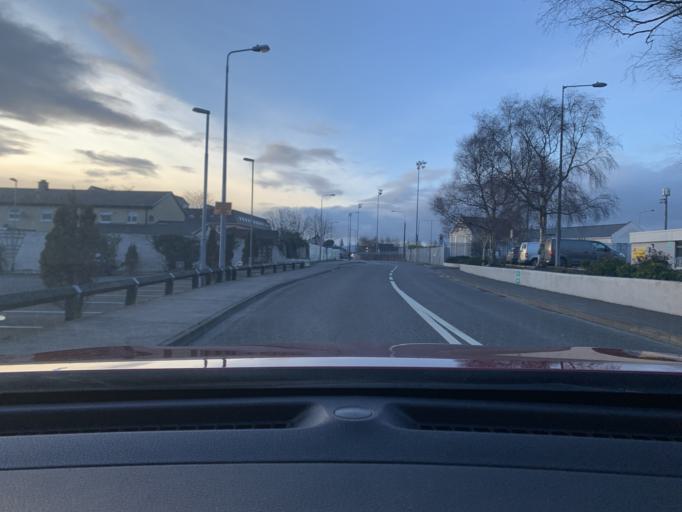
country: IE
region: Connaught
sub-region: Sligo
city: Sligo
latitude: 54.2676
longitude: -8.4609
